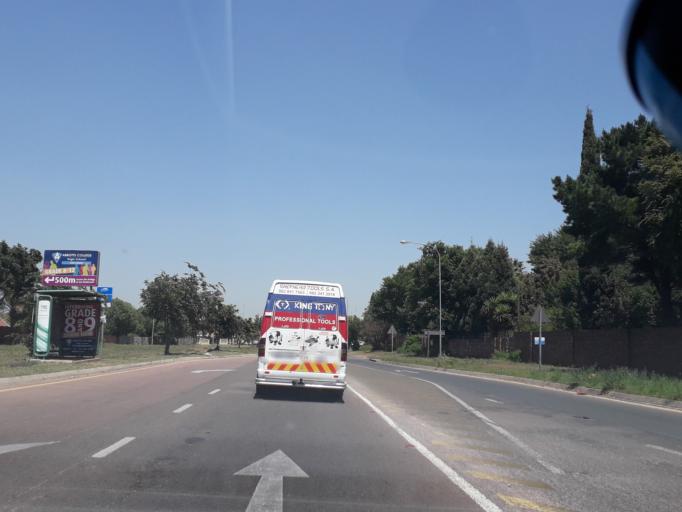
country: ZA
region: Gauteng
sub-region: City of Tshwane Metropolitan Municipality
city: Centurion
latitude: -25.8713
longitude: 28.1757
